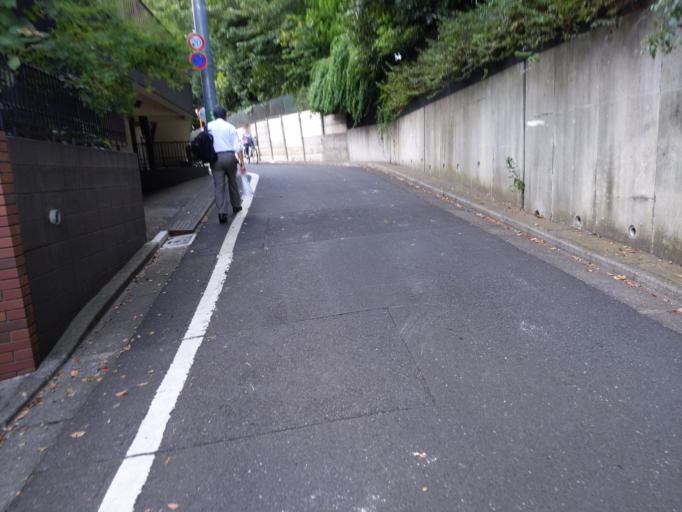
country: JP
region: Saitama
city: Wako
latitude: 35.7430
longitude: 139.6446
